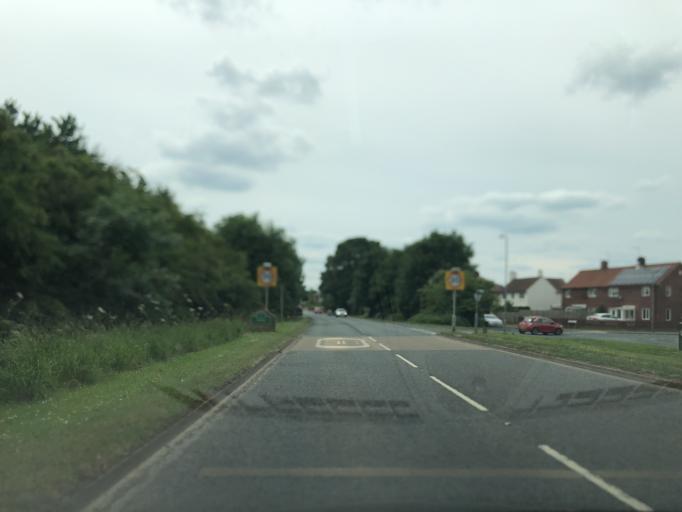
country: GB
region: England
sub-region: North Yorkshire
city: Thirsk
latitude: 54.2338
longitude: -1.3310
